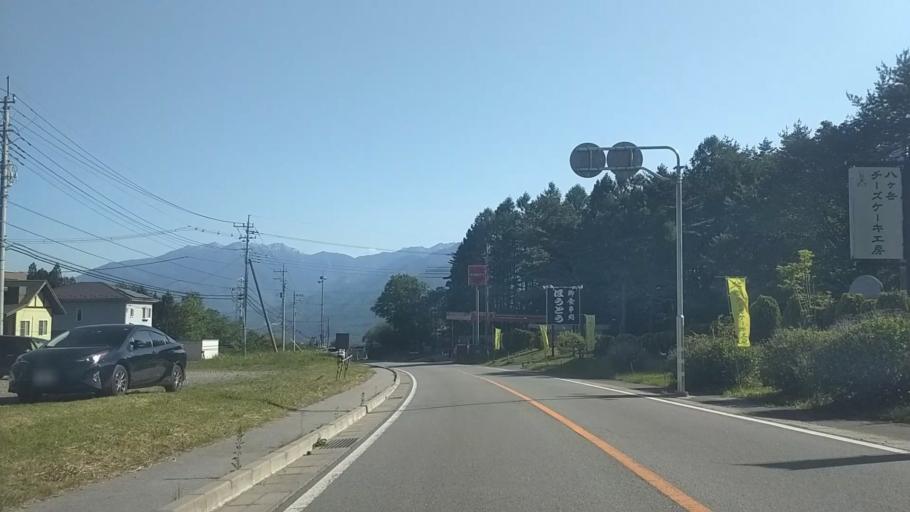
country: JP
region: Nagano
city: Chino
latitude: 35.8765
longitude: 138.3124
